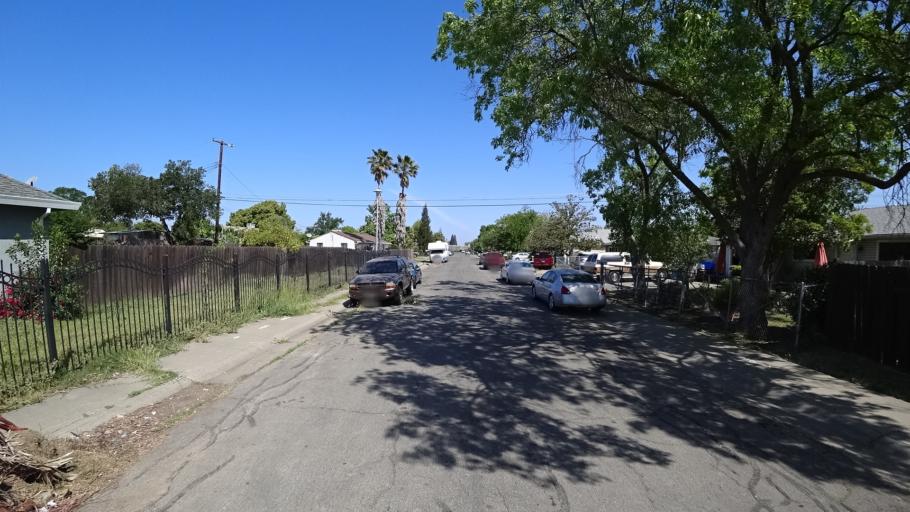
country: US
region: California
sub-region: Sacramento County
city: Parkway
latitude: 38.5050
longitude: -121.4756
